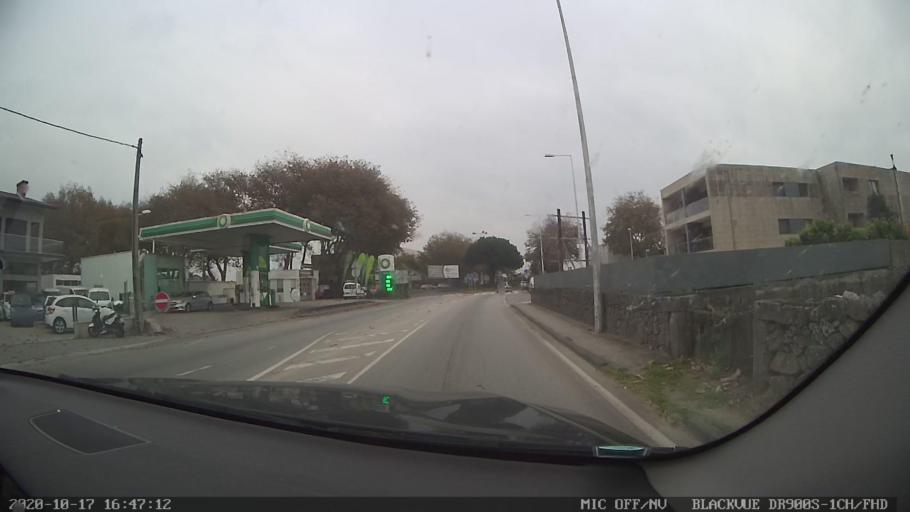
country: PT
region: Braga
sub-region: Esposende
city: Esposende
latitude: 41.5322
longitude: -8.7763
